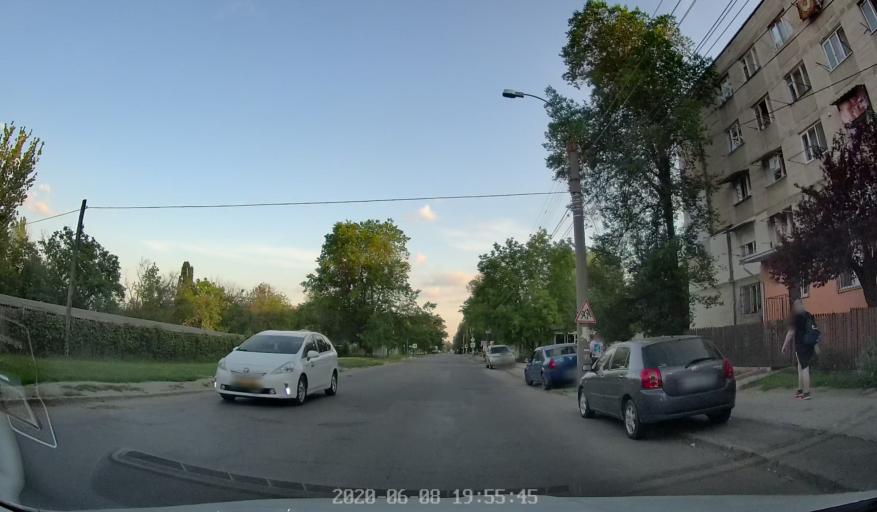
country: MD
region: Chisinau
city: Chisinau
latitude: 47.0267
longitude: 28.8836
